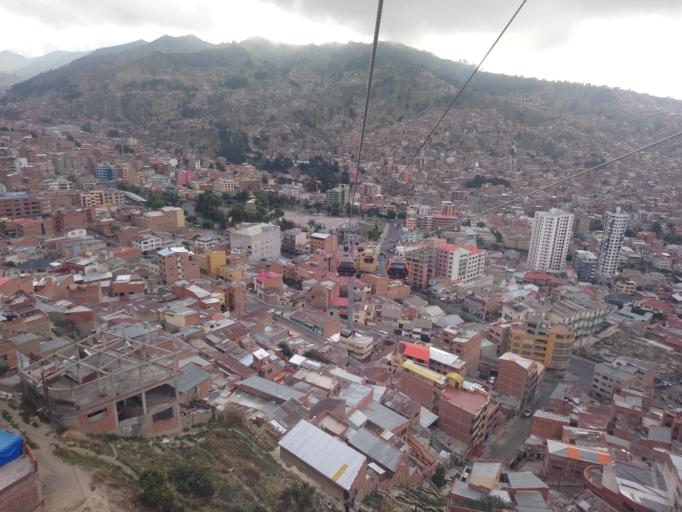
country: BO
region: La Paz
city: La Paz
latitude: -16.4854
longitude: -68.1260
